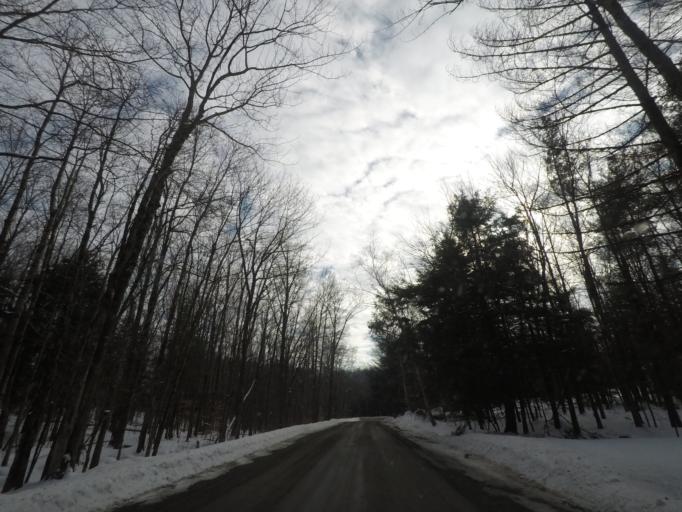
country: US
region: New York
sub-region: Rensselaer County
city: Averill Park
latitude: 42.6278
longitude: -73.5022
